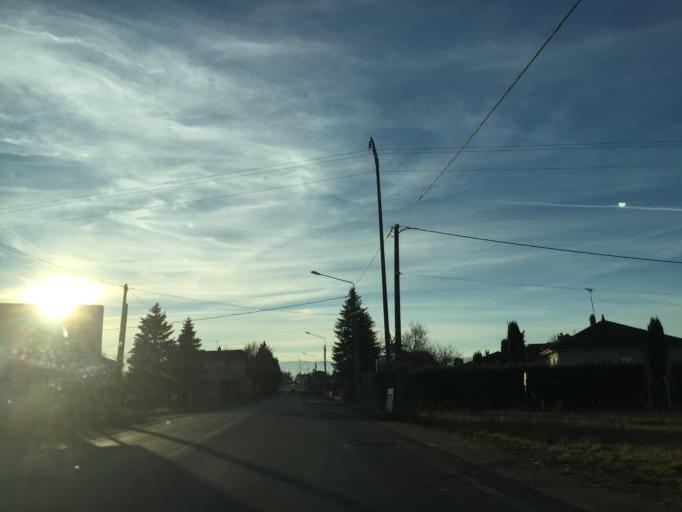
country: FR
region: Rhone-Alpes
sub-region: Departement de la Loire
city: Saint-Cyprien
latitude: 45.5283
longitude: 4.2404
